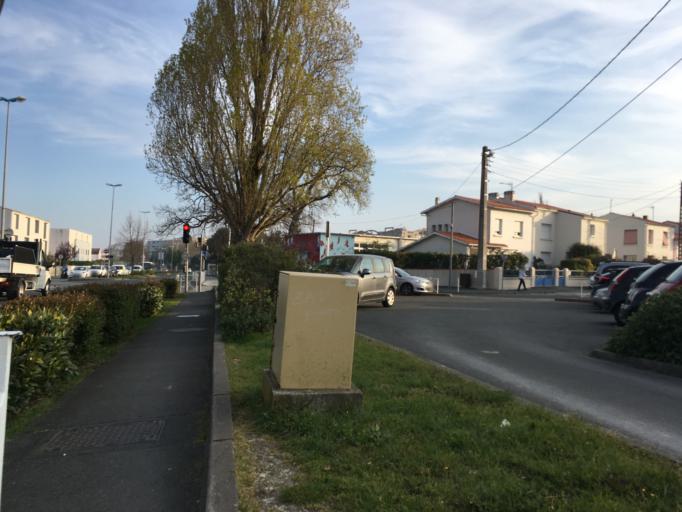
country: FR
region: Poitou-Charentes
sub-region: Departement de la Charente-Maritime
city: La Rochelle
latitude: 46.1729
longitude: -1.1503
